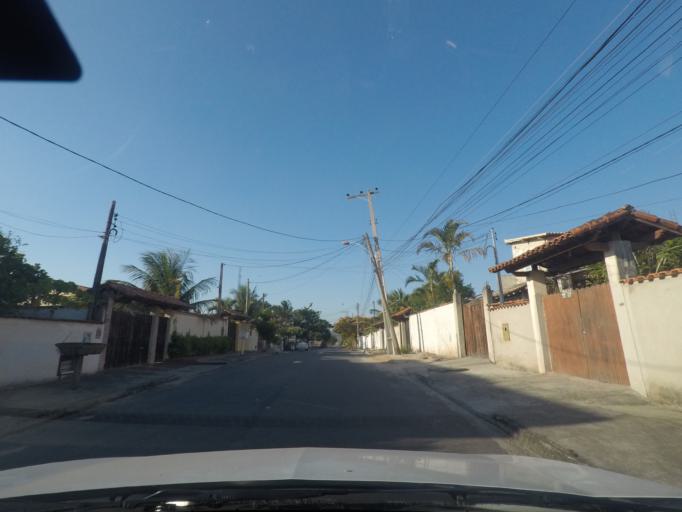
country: BR
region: Rio de Janeiro
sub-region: Marica
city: Marica
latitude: -22.9682
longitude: -42.9370
